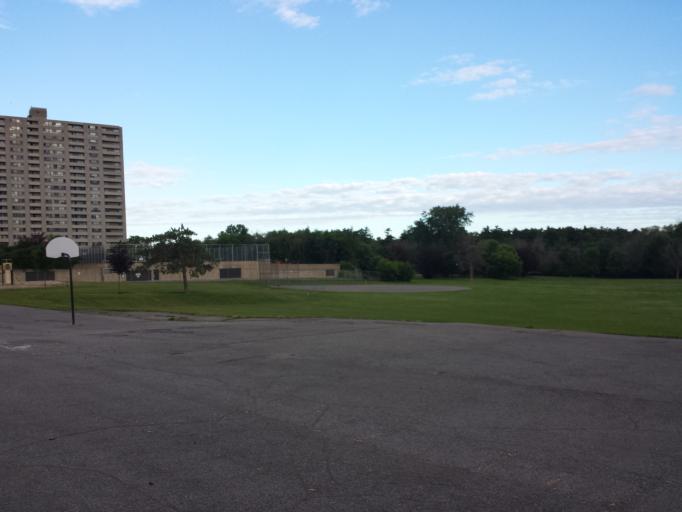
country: CA
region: Ontario
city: Bells Corners
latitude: 45.3672
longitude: -75.7900
